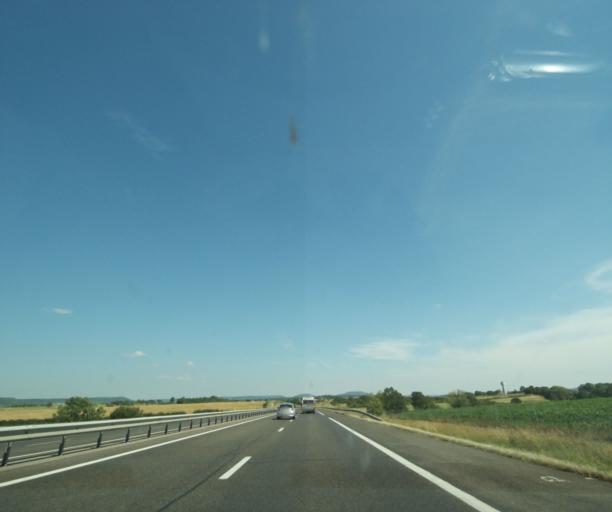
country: FR
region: Lorraine
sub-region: Departement de Meurthe-et-Moselle
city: Blenod-les-Toul
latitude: 48.5946
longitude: 5.8874
